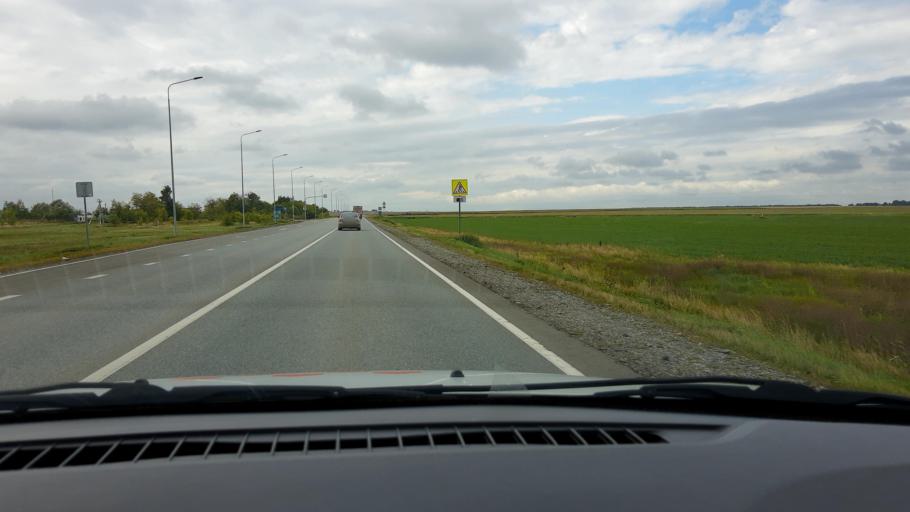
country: RU
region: Tatarstan
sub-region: Alekseyevskiy Rayon
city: Alekseyevskoye
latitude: 55.3132
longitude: 50.2892
